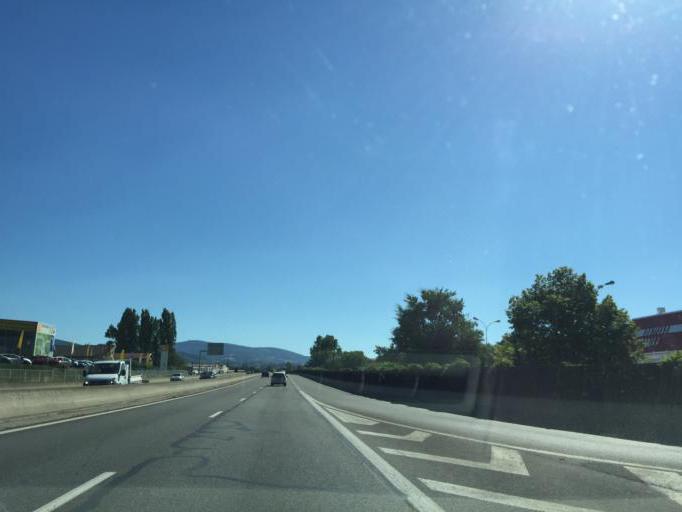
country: FR
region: Rhone-Alpes
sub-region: Departement de la Loire
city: Lorette
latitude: 45.5040
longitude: 4.5664
